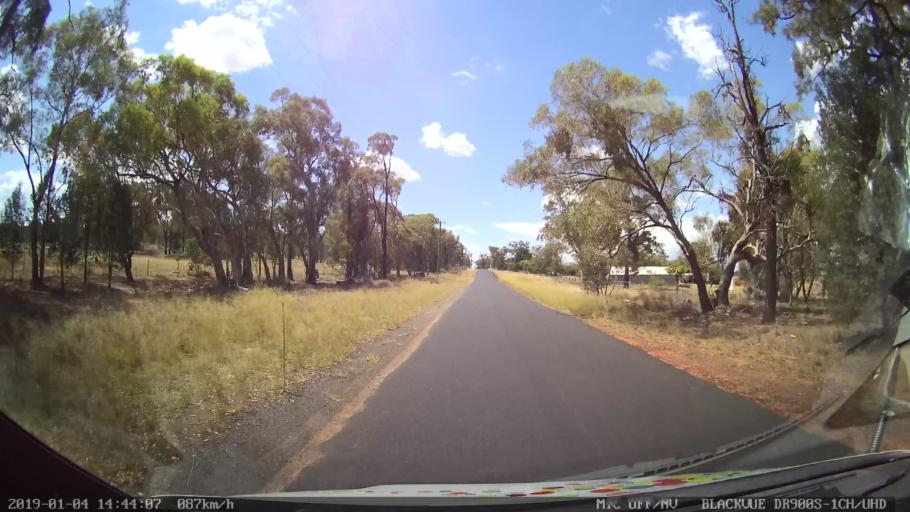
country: AU
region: New South Wales
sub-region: Dubbo Municipality
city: Dubbo
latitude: -32.1103
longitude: 148.6549
